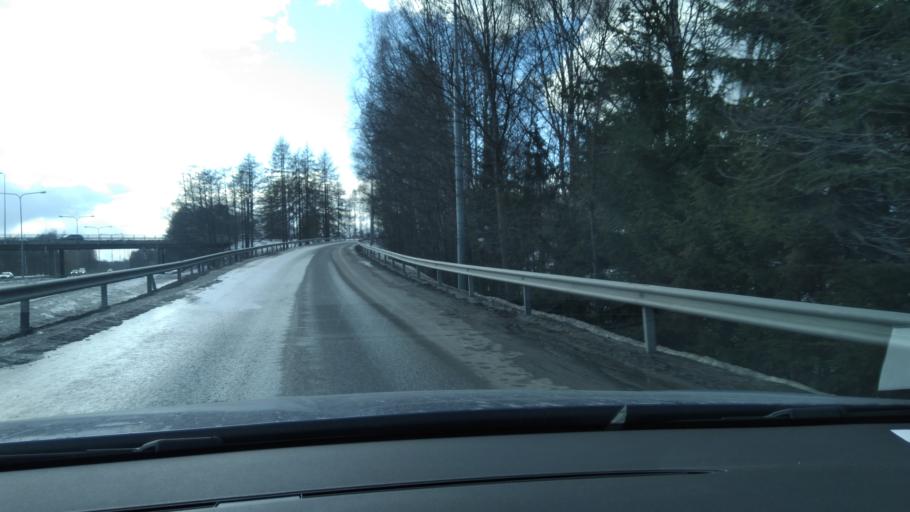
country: FI
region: Pirkanmaa
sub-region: Tampere
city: Pirkkala
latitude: 61.4983
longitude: 23.6569
